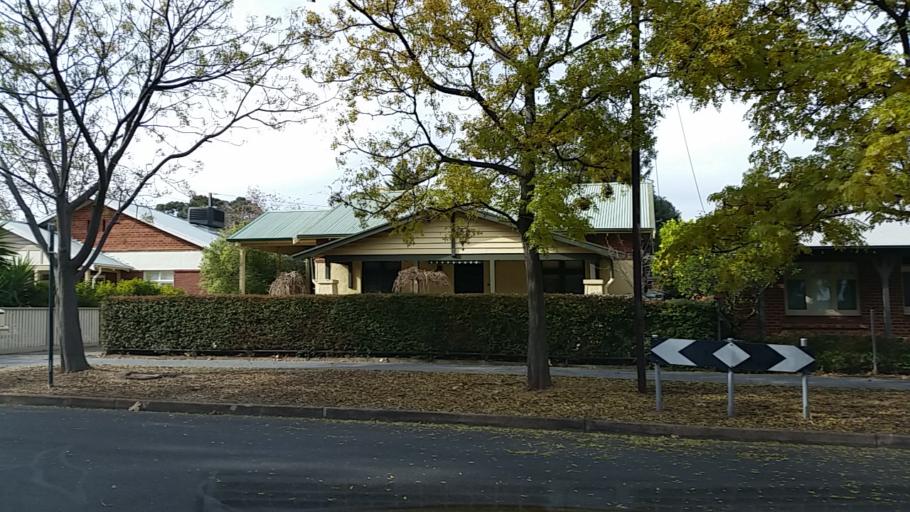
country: AU
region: South Australia
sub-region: Mitcham
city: Clapham
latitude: -34.9841
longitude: 138.5908
